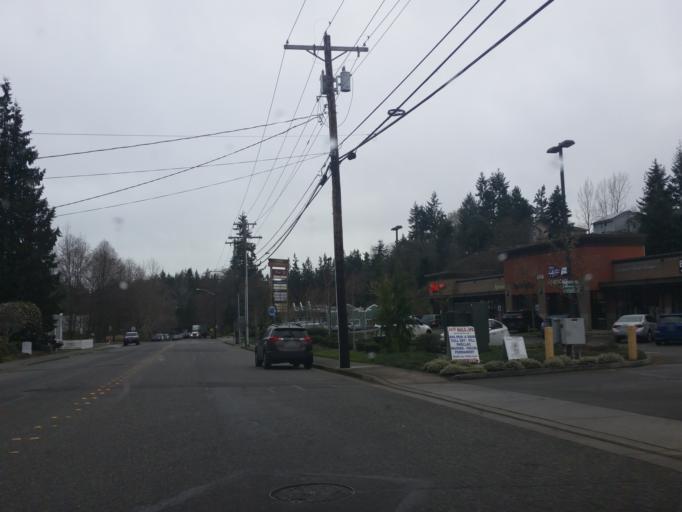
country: US
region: Washington
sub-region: Snohomish County
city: Meadowdale
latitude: 47.8303
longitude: -122.3376
